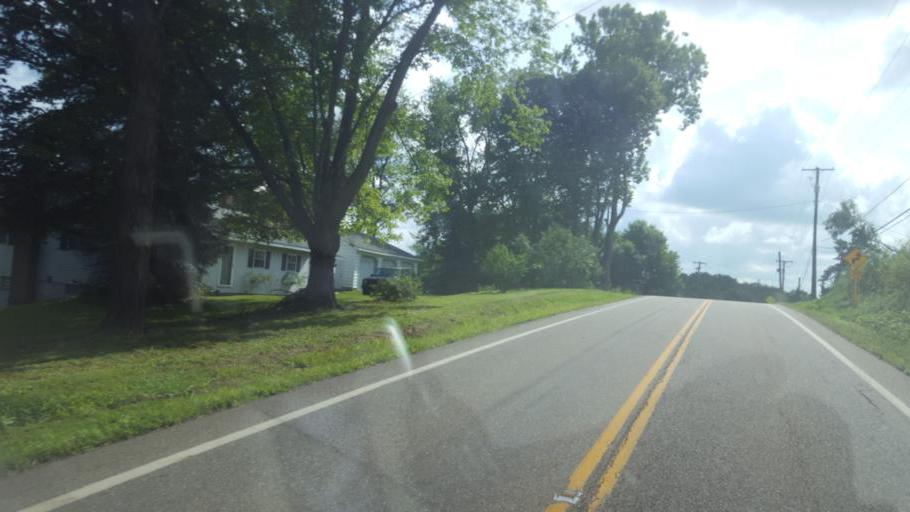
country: US
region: Ohio
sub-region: Columbiana County
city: Salem
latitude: 40.7938
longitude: -80.8817
